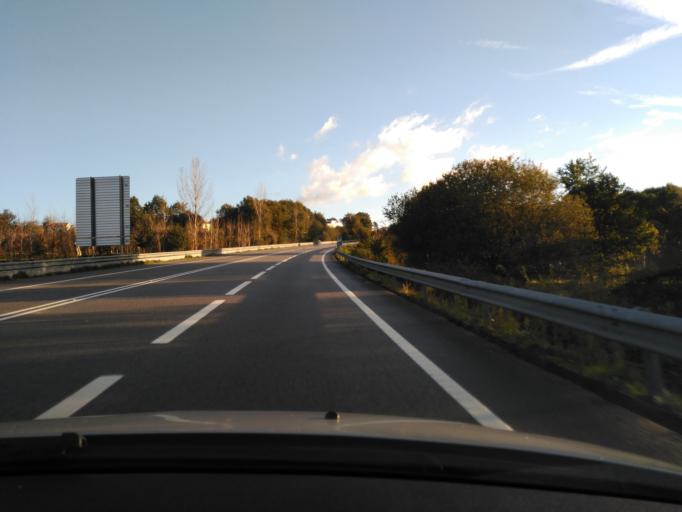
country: PT
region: Braga
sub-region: Fafe
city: Fafe
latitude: 41.4625
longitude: -8.1805
